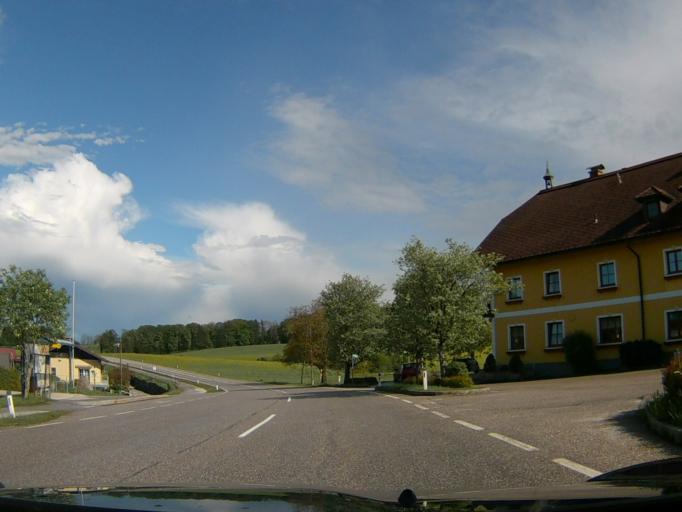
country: AT
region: Salzburg
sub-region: Politischer Bezirk Salzburg-Umgebung
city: Plainfeld
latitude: 47.8555
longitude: 13.1782
